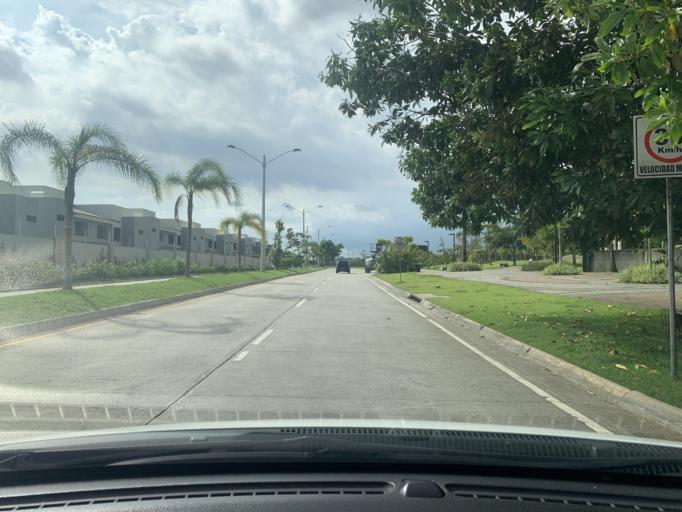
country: PA
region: Panama
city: San Miguelito
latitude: 9.0913
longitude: -79.4687
